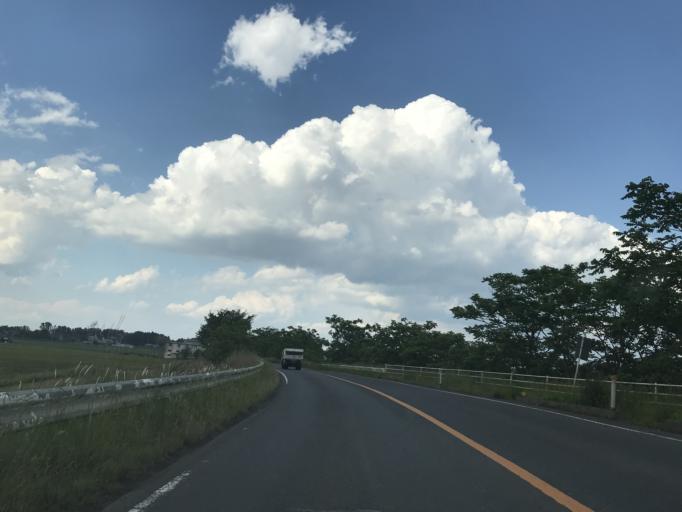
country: JP
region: Miyagi
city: Wakuya
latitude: 38.5883
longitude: 141.1615
